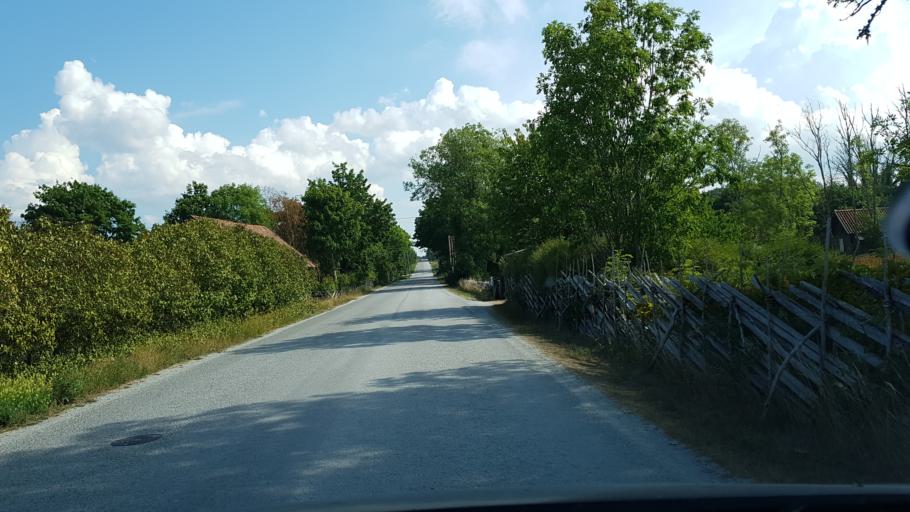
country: SE
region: Gotland
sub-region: Gotland
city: Visby
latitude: 57.8239
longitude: 18.5148
